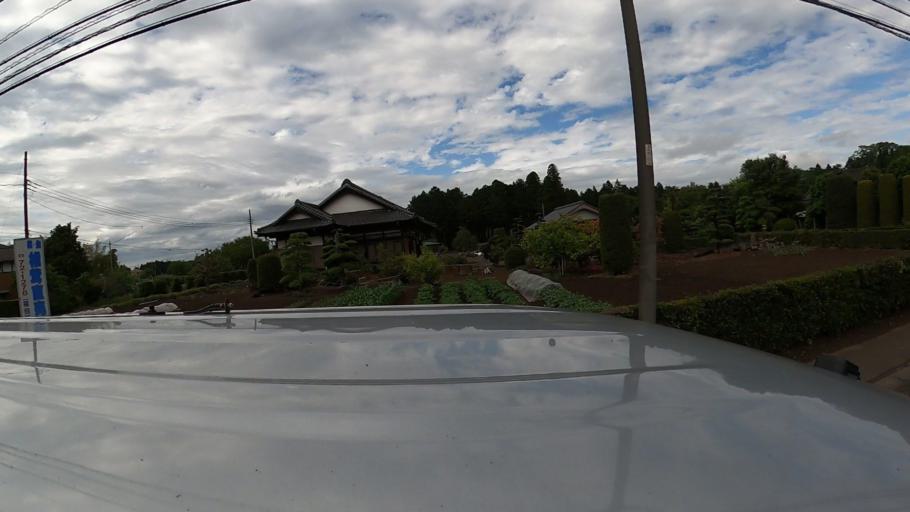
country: JP
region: Ibaraki
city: Ushiku
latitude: 35.9758
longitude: 140.1794
